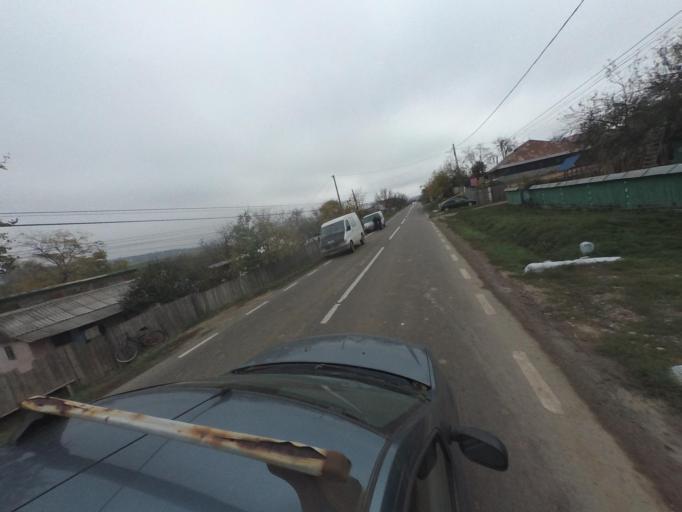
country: RO
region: Vaslui
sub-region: Comuna Bacesti
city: Bacesti
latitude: 46.8324
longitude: 27.2341
